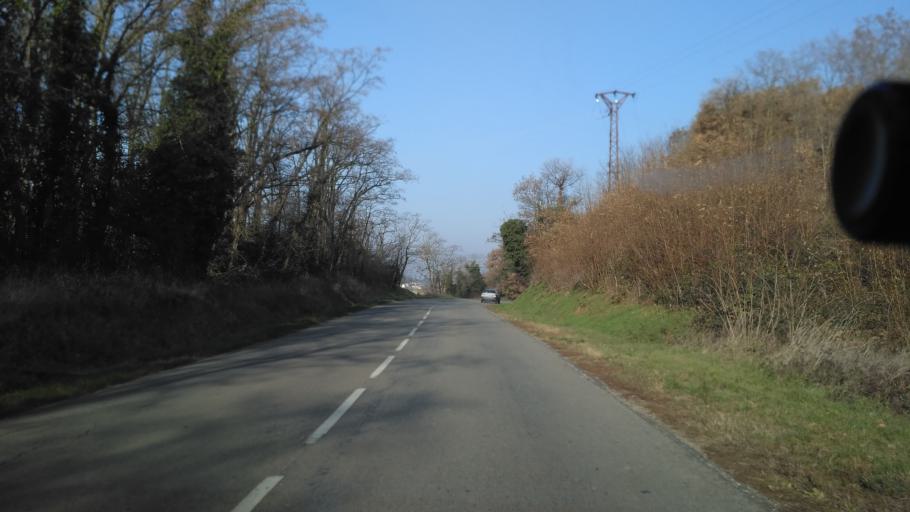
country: FR
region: Rhone-Alpes
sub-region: Departement de la Drome
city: Clerieux
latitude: 45.0620
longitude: 4.9641
